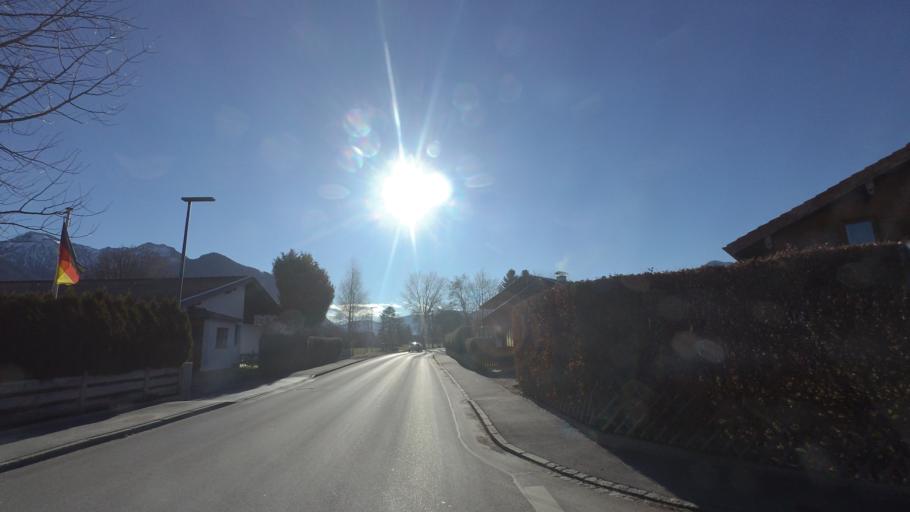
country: DE
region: Bavaria
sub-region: Upper Bavaria
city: Staudach-Egerndach
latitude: 47.7945
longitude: 12.4721
